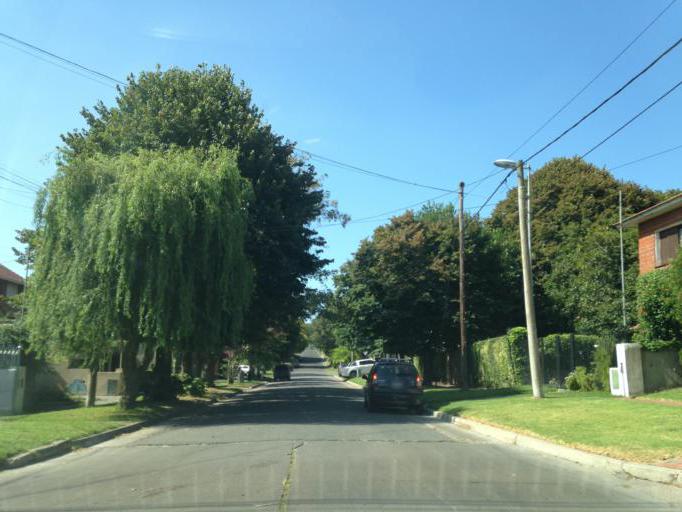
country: AR
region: Buenos Aires
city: Mar del Plata
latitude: -38.0326
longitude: -57.5483
